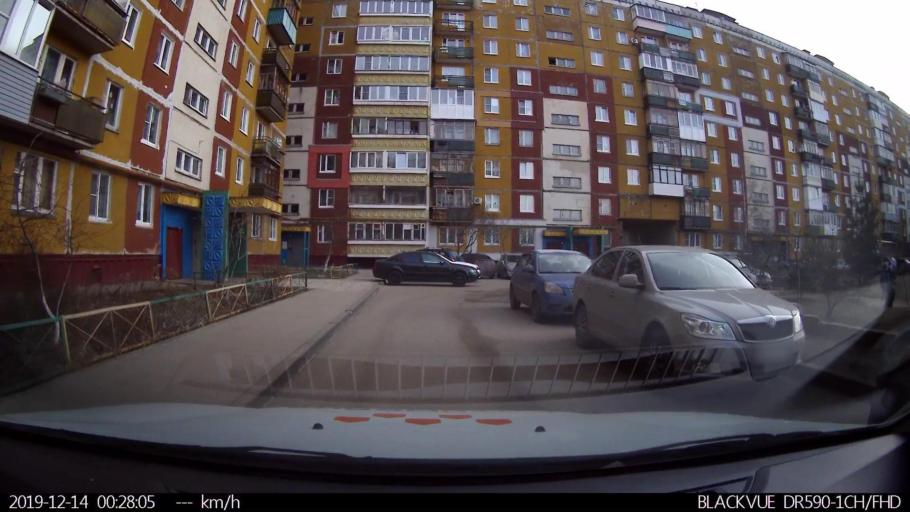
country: RU
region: Nizjnij Novgorod
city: Burevestnik
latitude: 56.2203
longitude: 43.8403
